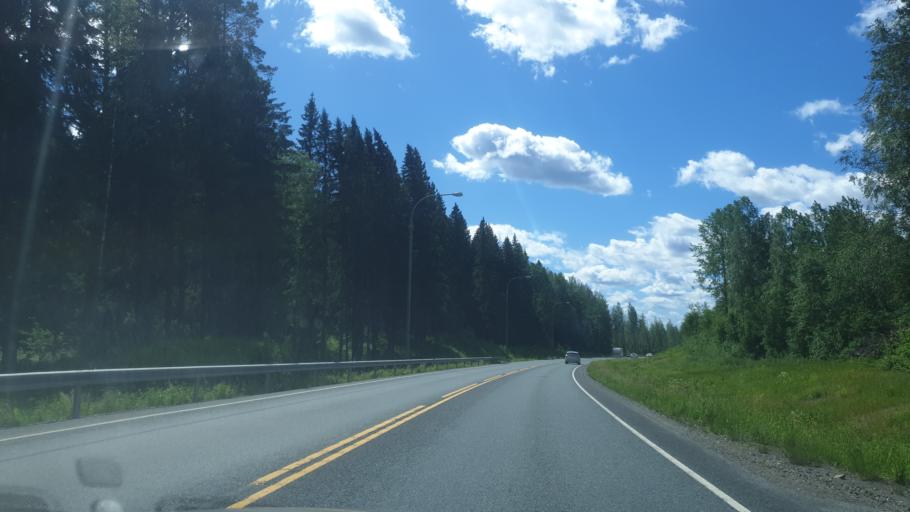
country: FI
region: Northern Savo
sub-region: Varkaus
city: Leppaevirta
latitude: 62.6069
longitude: 27.6223
